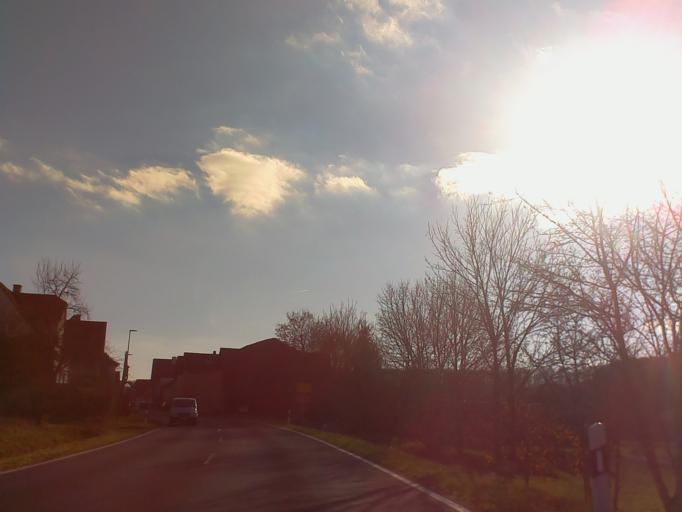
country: DE
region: Bavaria
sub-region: Regierungsbezirk Unterfranken
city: Bad Bocklet
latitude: 50.2489
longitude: 10.0646
